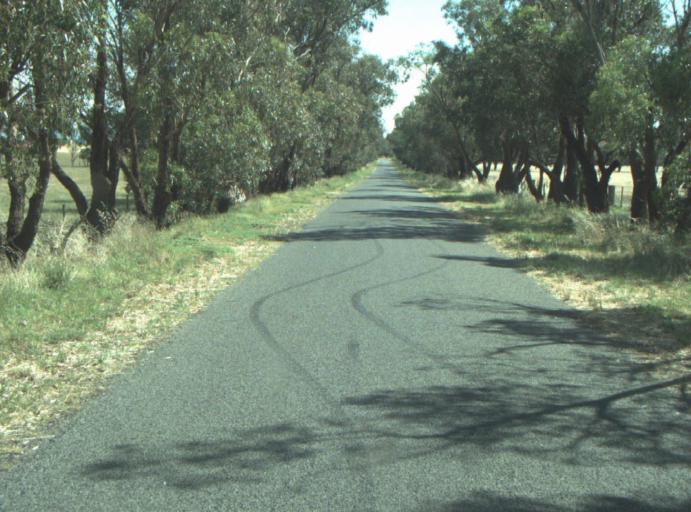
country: AU
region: Victoria
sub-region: Greater Geelong
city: Leopold
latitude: -38.1701
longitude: 144.4720
